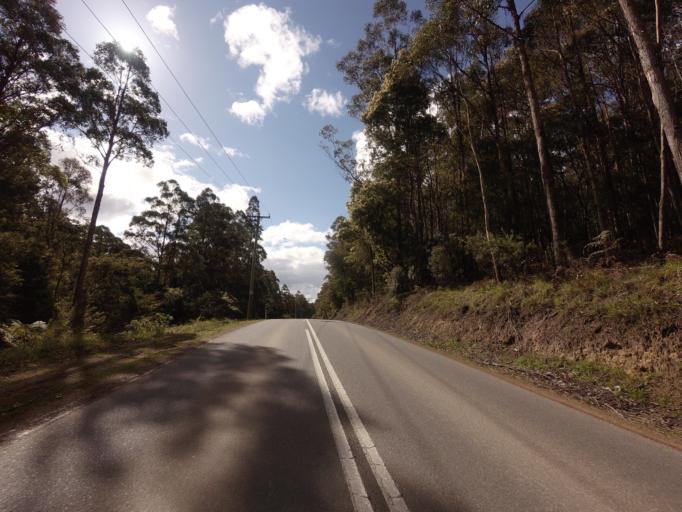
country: AU
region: Tasmania
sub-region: Huon Valley
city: Geeveston
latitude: -43.2292
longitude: 146.9881
